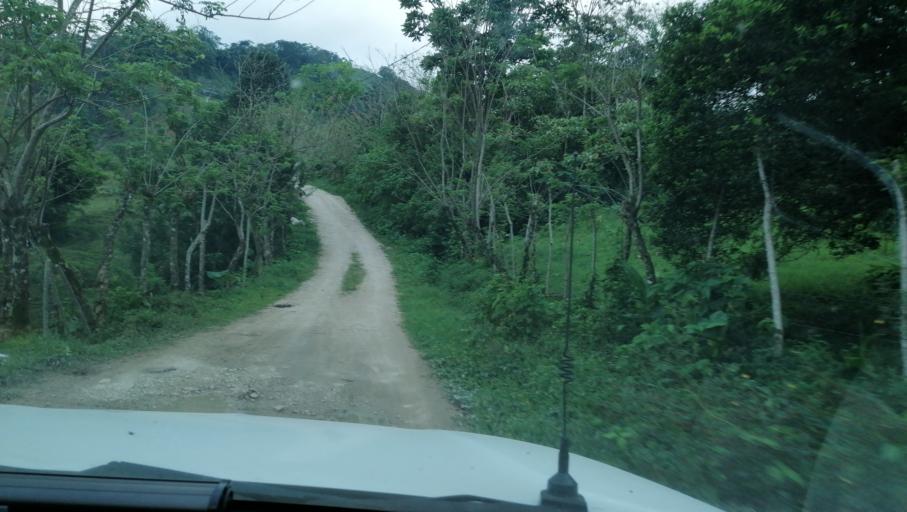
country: MX
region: Chiapas
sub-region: Francisco Leon
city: San Miguel la Sardina
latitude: 17.3062
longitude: -93.2672
